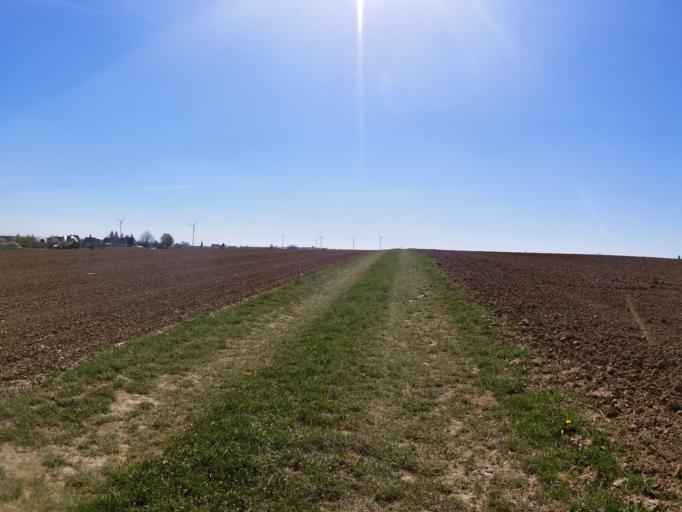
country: DE
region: Bavaria
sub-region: Regierungsbezirk Unterfranken
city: Biebelried
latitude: 49.8034
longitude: 10.1011
